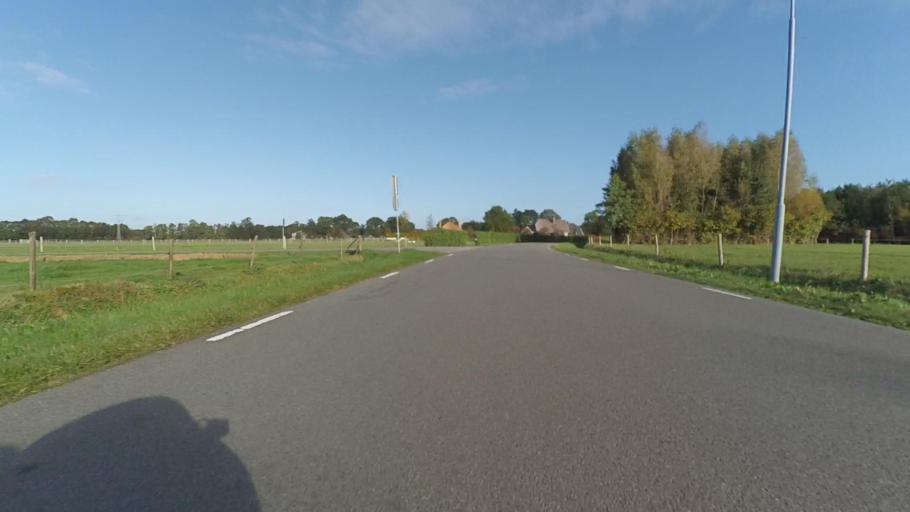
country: NL
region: Gelderland
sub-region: Gemeente Ermelo
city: Horst
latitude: 52.2967
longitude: 5.5774
